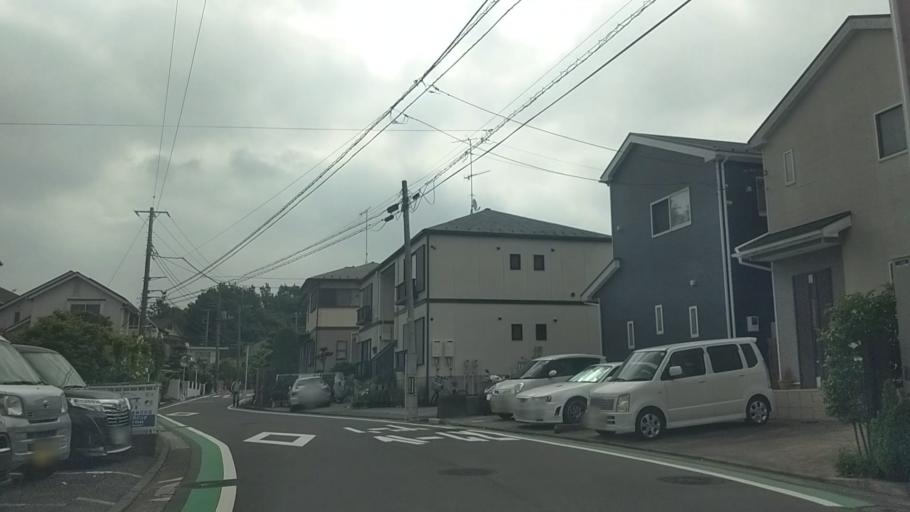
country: JP
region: Kanagawa
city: Kamakura
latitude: 35.3770
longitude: 139.5378
